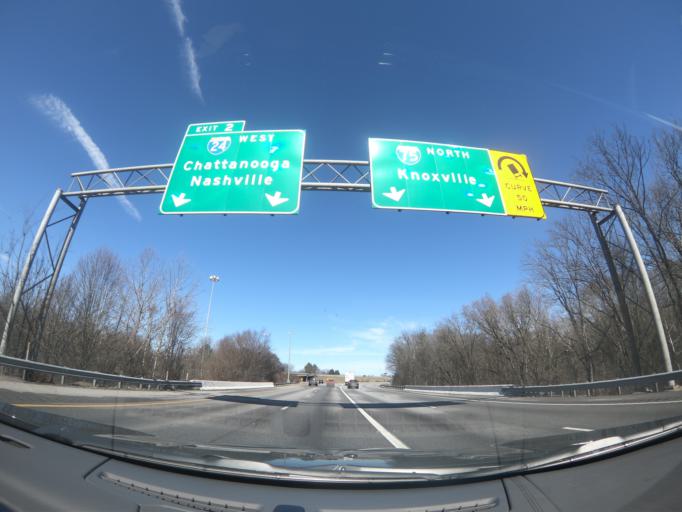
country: US
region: Tennessee
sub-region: Hamilton County
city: East Ridge
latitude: 35.0010
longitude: -85.2108
